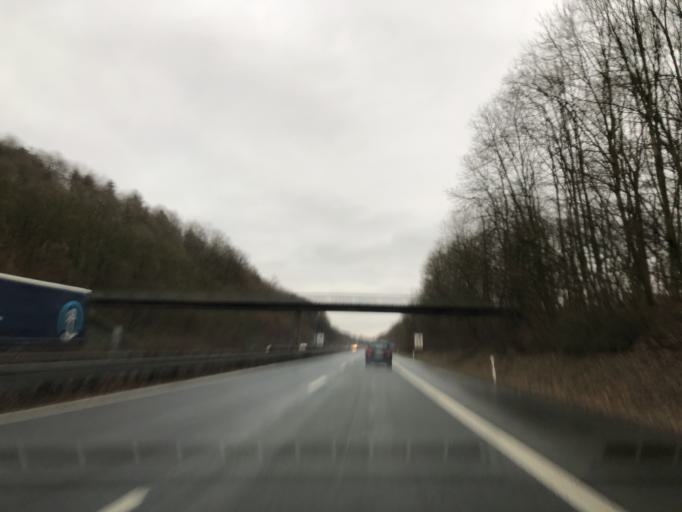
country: DE
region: North Rhine-Westphalia
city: Iserlohn
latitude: 51.3882
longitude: 7.7188
